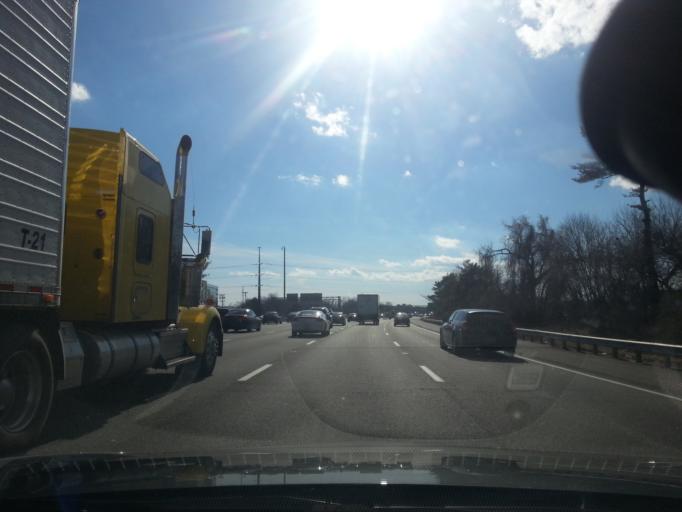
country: US
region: Delaware
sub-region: New Castle County
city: Newport
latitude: 39.6980
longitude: -75.6141
